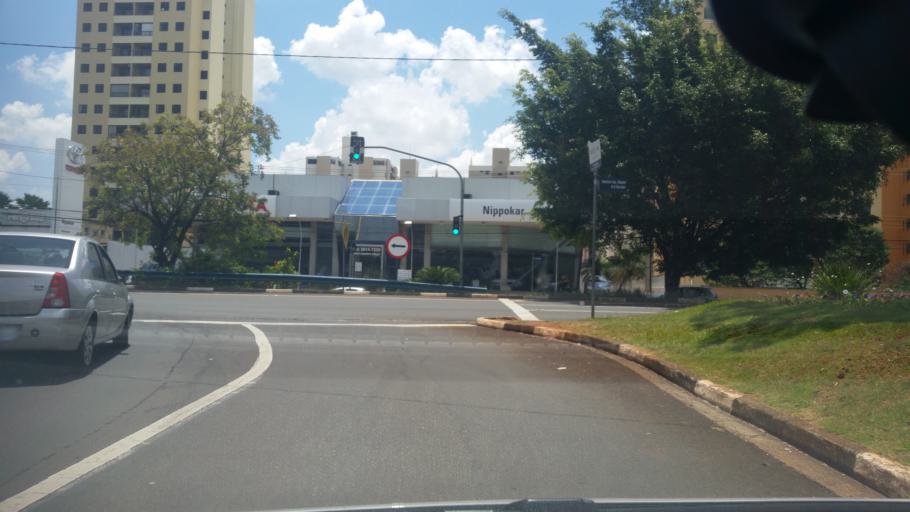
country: BR
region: Sao Paulo
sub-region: Campinas
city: Campinas
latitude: -22.8555
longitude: -47.0442
